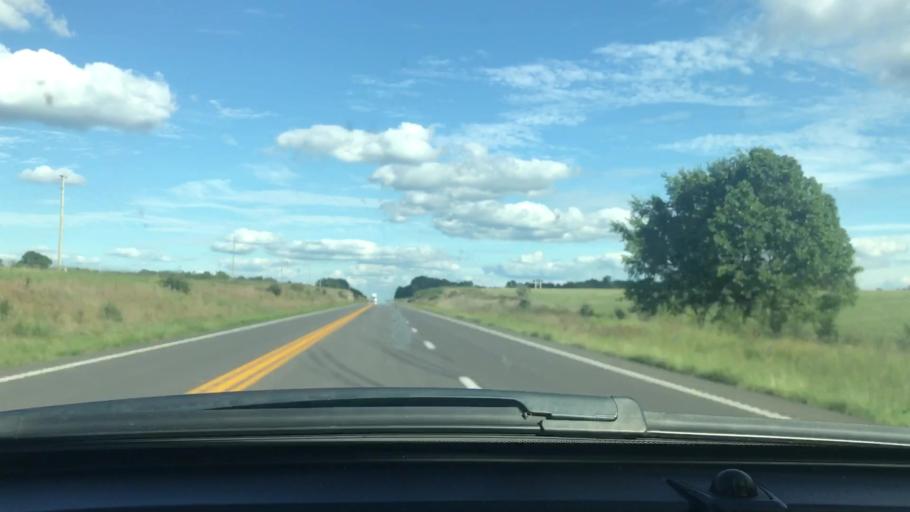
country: US
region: Missouri
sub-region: Oregon County
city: Thayer
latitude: 36.5852
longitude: -91.6226
